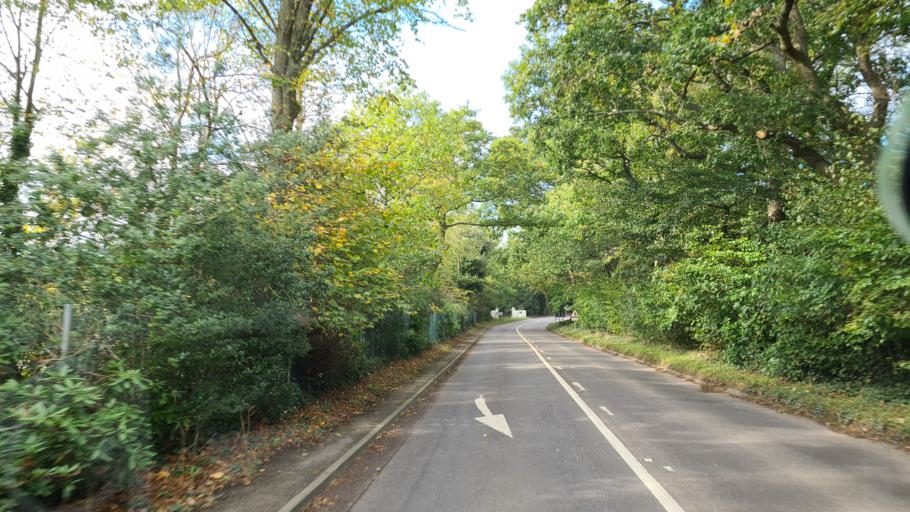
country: GB
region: England
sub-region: East Sussex
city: Bodle Street
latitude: 50.8822
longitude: 0.3549
